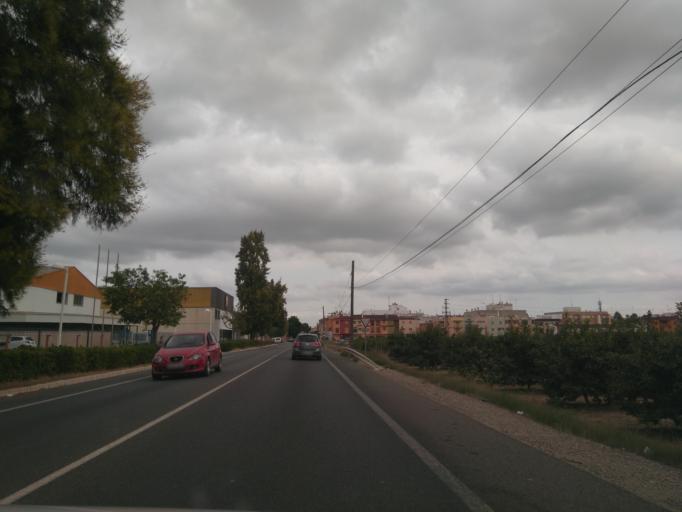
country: ES
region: Valencia
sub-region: Provincia de Valencia
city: L'Alcudia
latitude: 39.2036
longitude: -0.5074
